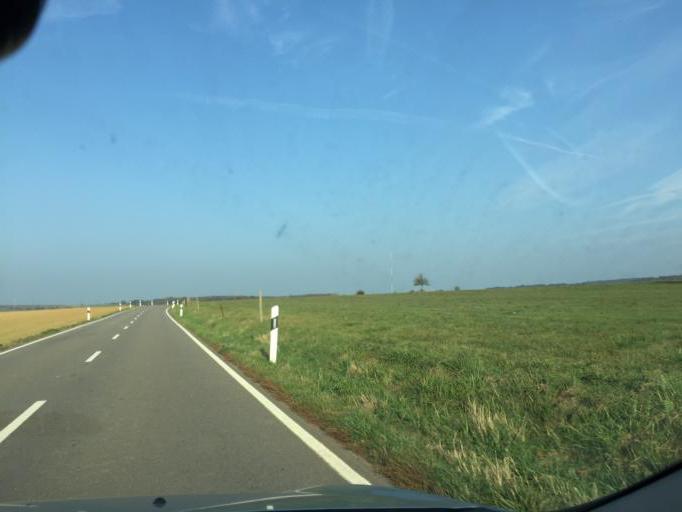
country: LU
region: Grevenmacher
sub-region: Canton de Remich
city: Dalheim
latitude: 49.5378
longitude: 6.2422
